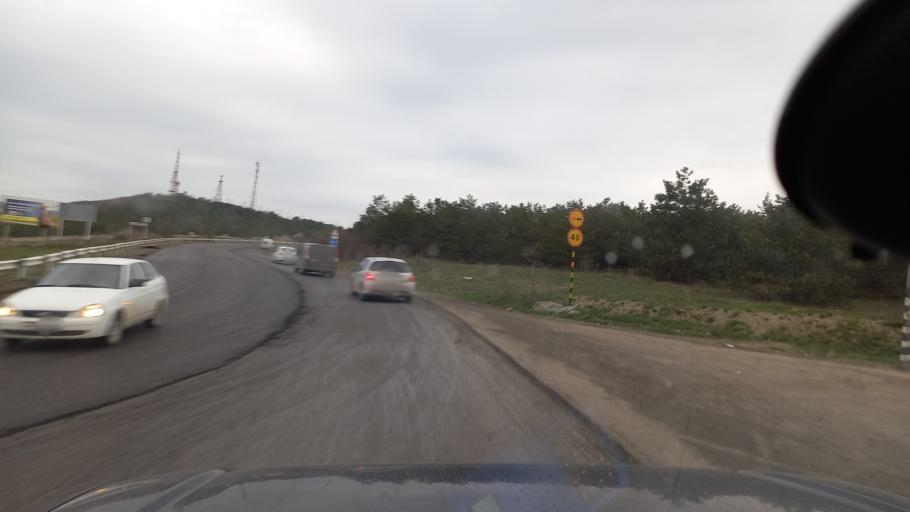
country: RU
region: Krasnodarskiy
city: Anapskaya
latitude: 44.8436
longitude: 37.3789
